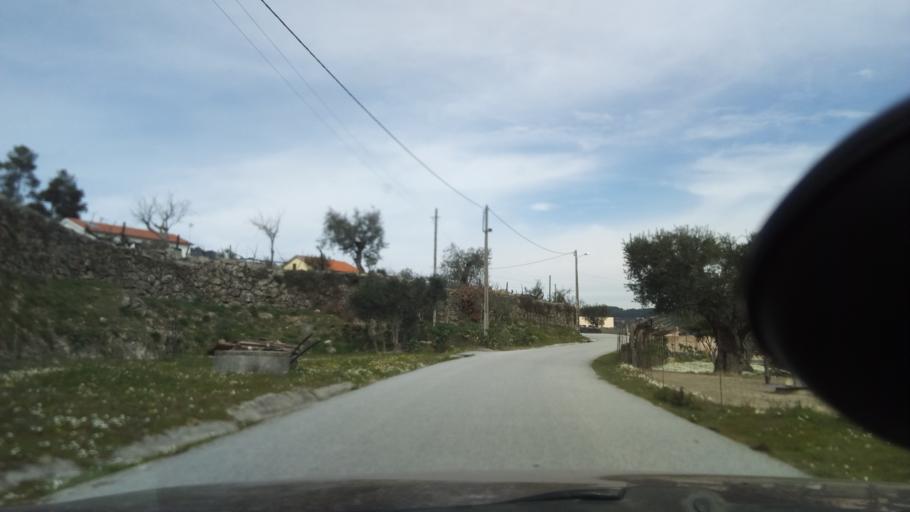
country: PT
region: Guarda
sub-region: Fornos de Algodres
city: Fornos de Algodres
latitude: 40.6113
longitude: -7.5386
